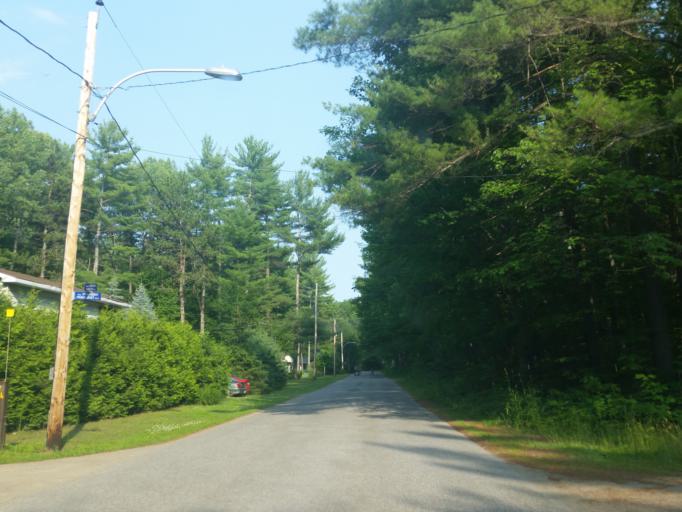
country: CA
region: Quebec
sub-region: Outaouais
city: Shawville
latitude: 45.5194
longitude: -76.4185
